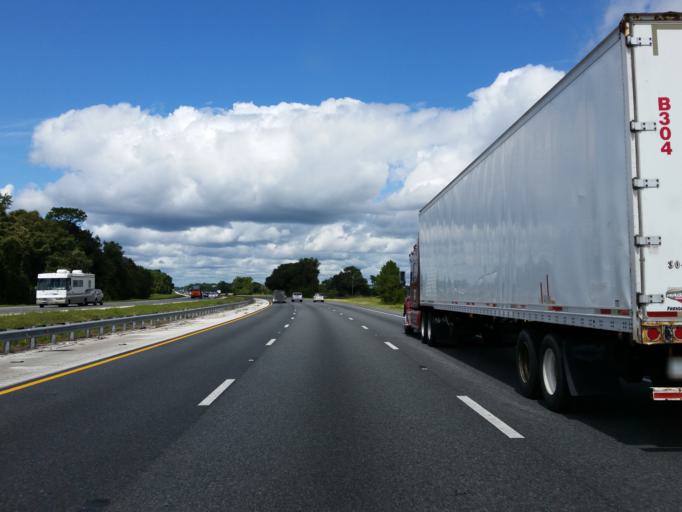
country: US
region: Florida
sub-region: Sumter County
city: Wildwood
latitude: 28.9376
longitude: -82.1123
